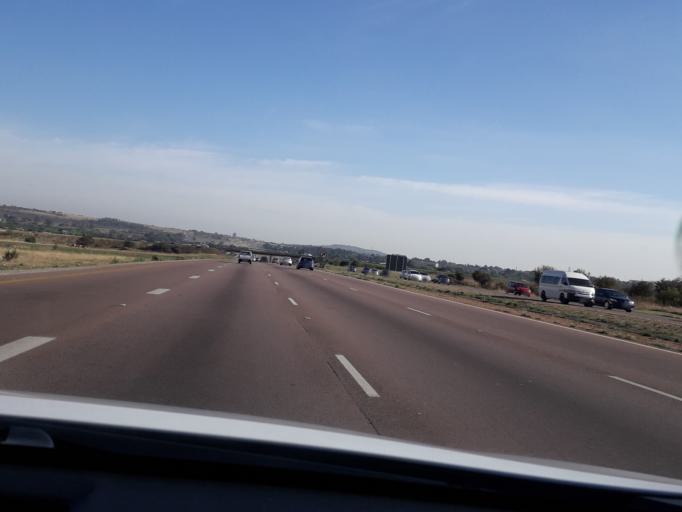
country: ZA
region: Gauteng
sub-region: City of Tshwane Metropolitan Municipality
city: Centurion
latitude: -25.8272
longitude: 28.1831
